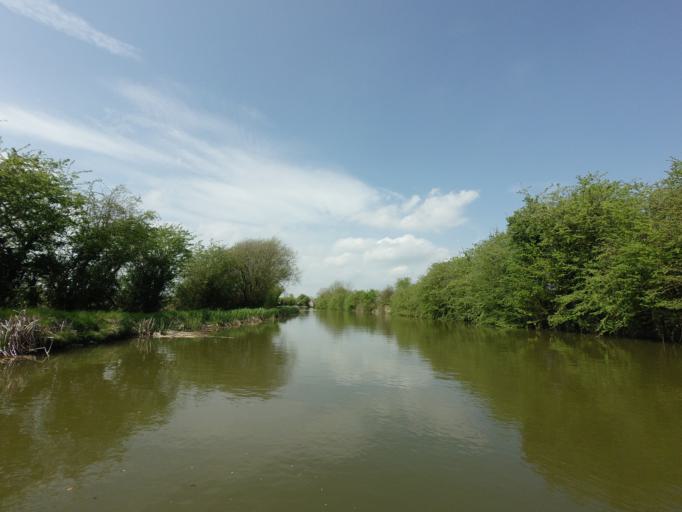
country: GB
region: England
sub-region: Buckinghamshire
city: Cheddington
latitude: 51.8781
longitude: -0.6572
